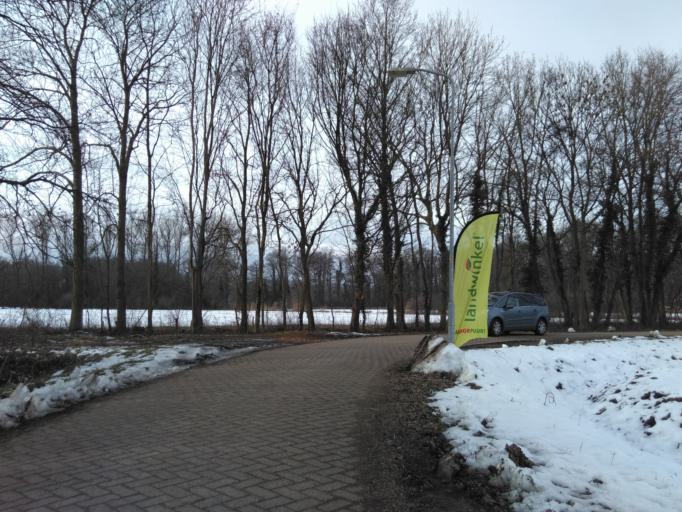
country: NL
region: Gelderland
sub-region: Gemeente Overbetuwe
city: Herveld
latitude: 51.8883
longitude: 5.7712
